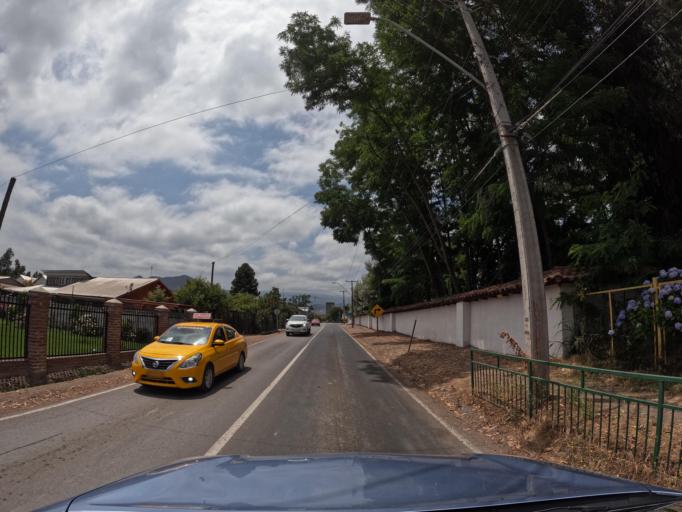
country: CL
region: O'Higgins
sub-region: Provincia de Colchagua
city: Chimbarongo
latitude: -34.7353
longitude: -70.9767
